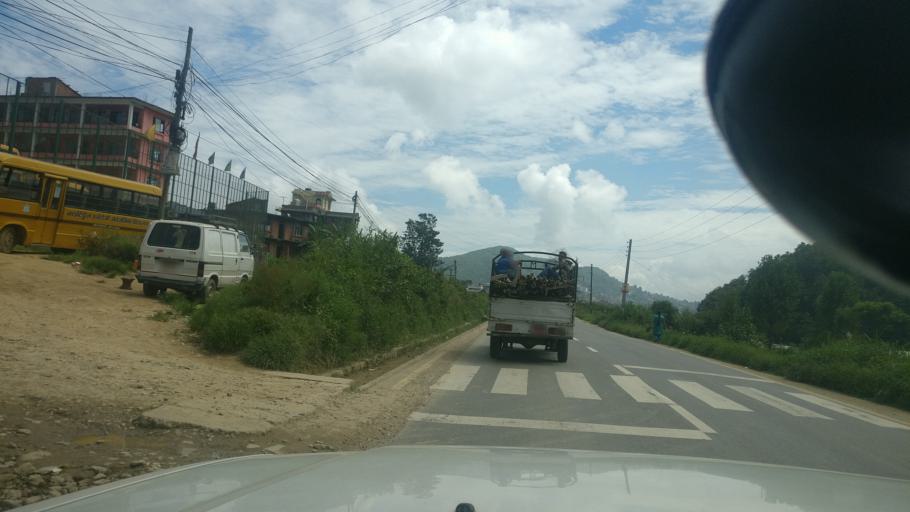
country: NP
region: Central Region
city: Banepa
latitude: 27.6316
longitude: 85.5057
